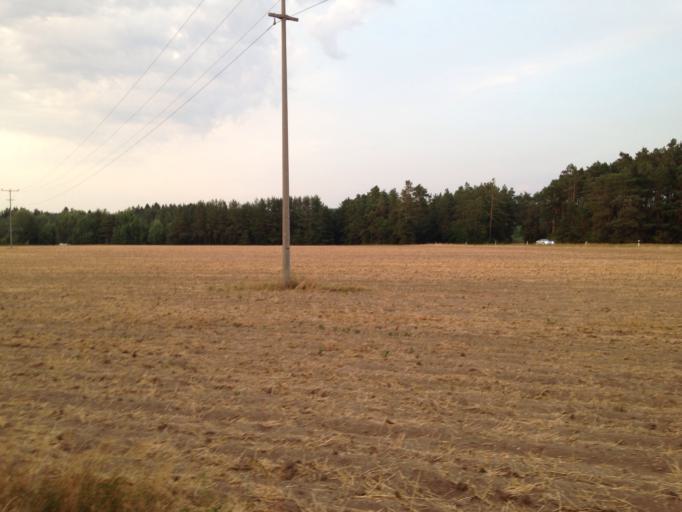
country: DE
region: Bavaria
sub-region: Regierungsbezirk Mittelfranken
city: Hilpoltstein
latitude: 49.1641
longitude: 11.1735
